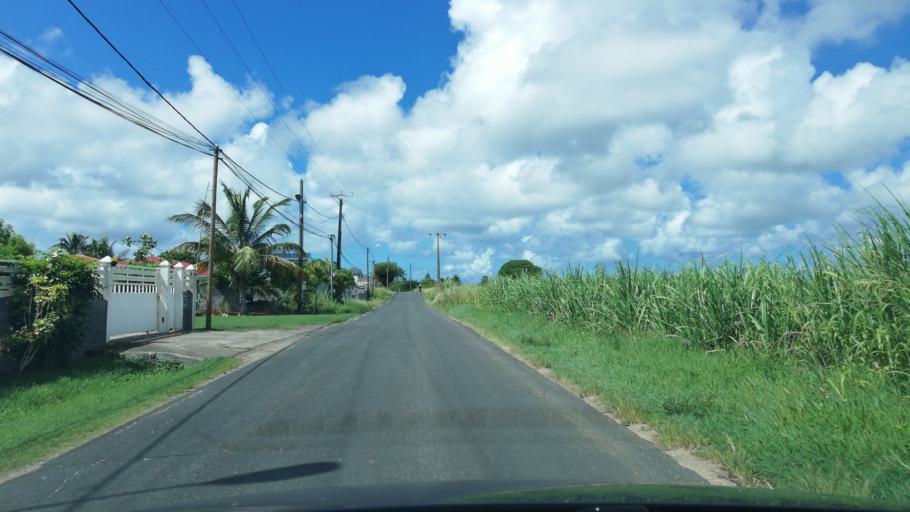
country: GP
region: Guadeloupe
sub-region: Guadeloupe
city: Petit-Canal
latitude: 16.3797
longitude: -61.4383
